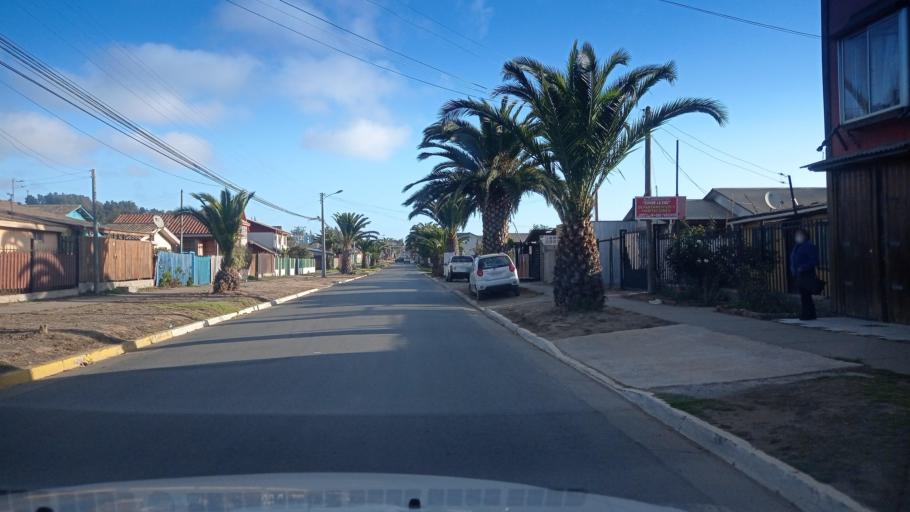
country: CL
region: O'Higgins
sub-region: Provincia de Colchagua
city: Santa Cruz
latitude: -34.3881
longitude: -72.0124
